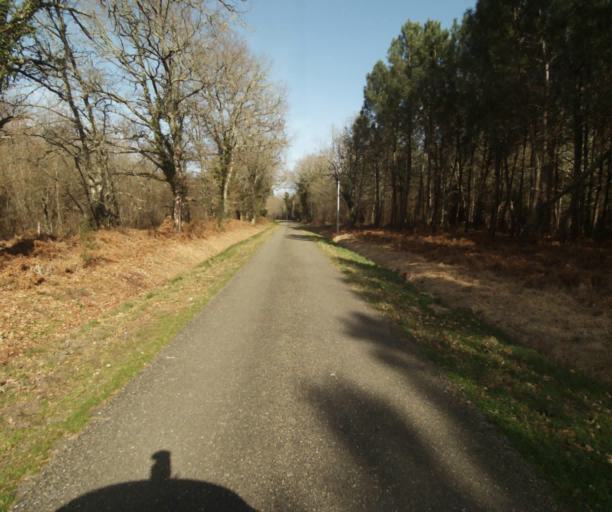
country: FR
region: Aquitaine
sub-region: Departement des Landes
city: Roquefort
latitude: 44.1539
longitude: -0.1972
